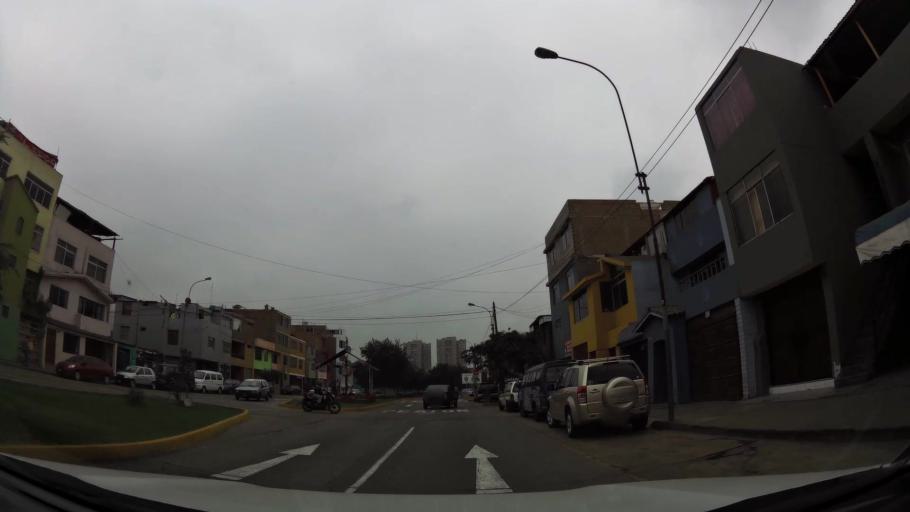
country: PE
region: Lima
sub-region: Lima
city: Surco
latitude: -12.1088
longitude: -77.0090
